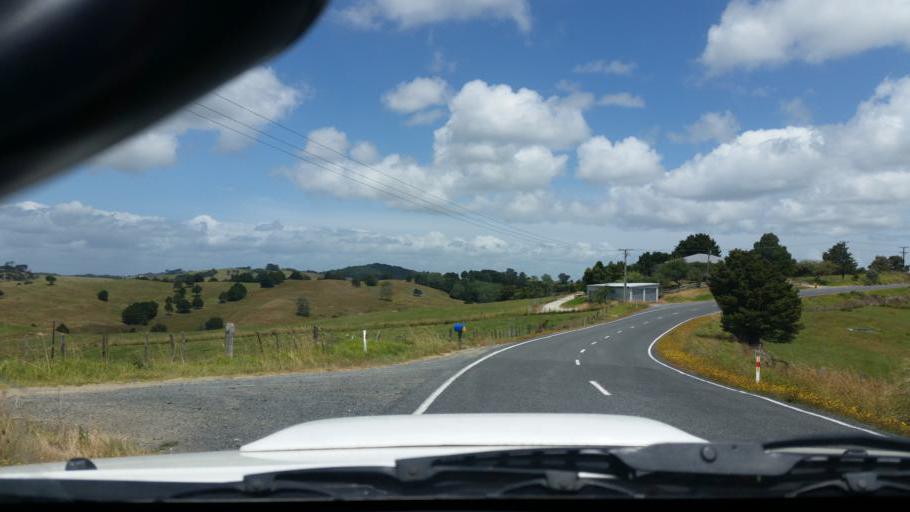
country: NZ
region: Northland
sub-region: Whangarei
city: Ruakaka
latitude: -36.0587
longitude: 174.2726
